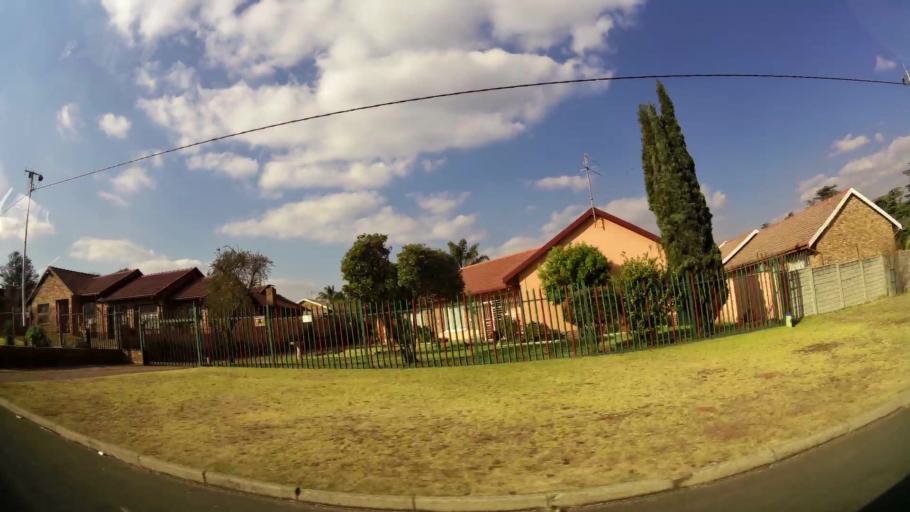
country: ZA
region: Gauteng
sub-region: West Rand District Municipality
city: Krugersdorp
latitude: -26.0915
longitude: 27.7635
